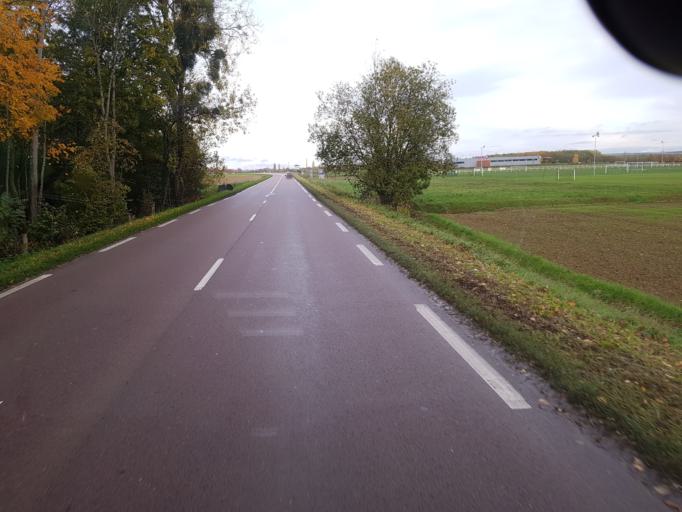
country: FR
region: Champagne-Ardenne
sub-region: Departement de l'Aube
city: Lusigny-sur-Barse
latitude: 48.2585
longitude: 4.2516
